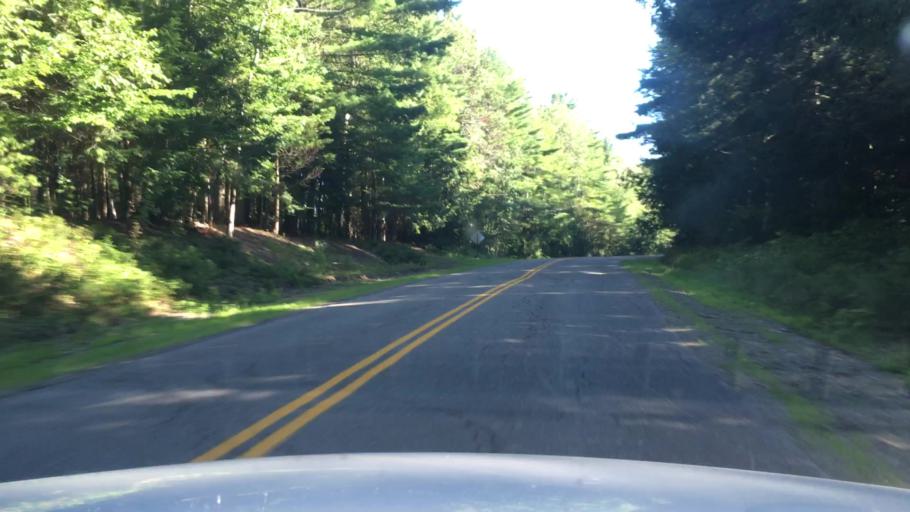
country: US
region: Maine
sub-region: Penobscot County
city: Enfield
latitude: 45.2234
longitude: -68.5801
